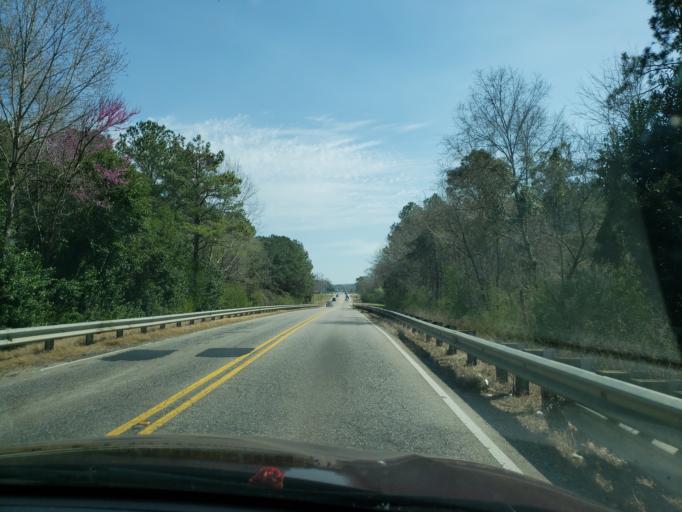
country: US
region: Alabama
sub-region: Elmore County
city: Elmore
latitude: 32.5408
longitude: -86.2681
